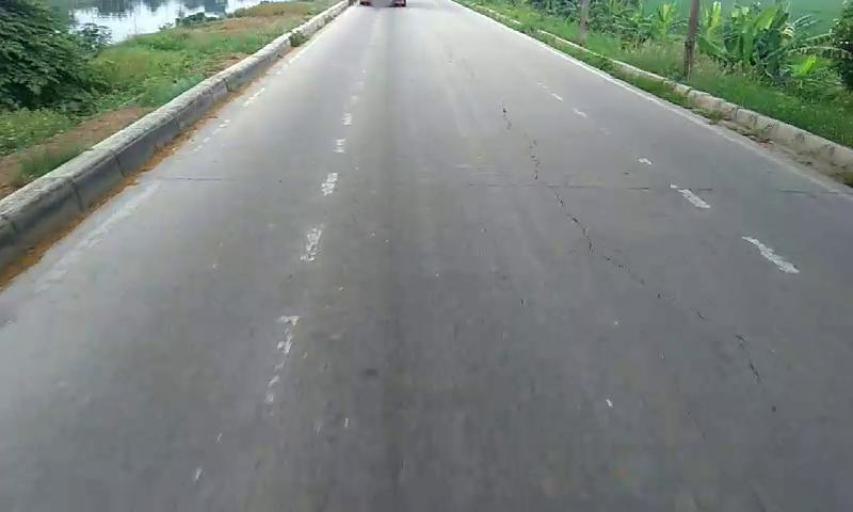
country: ID
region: West Java
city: Bekasi
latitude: -6.1484
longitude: 106.9703
